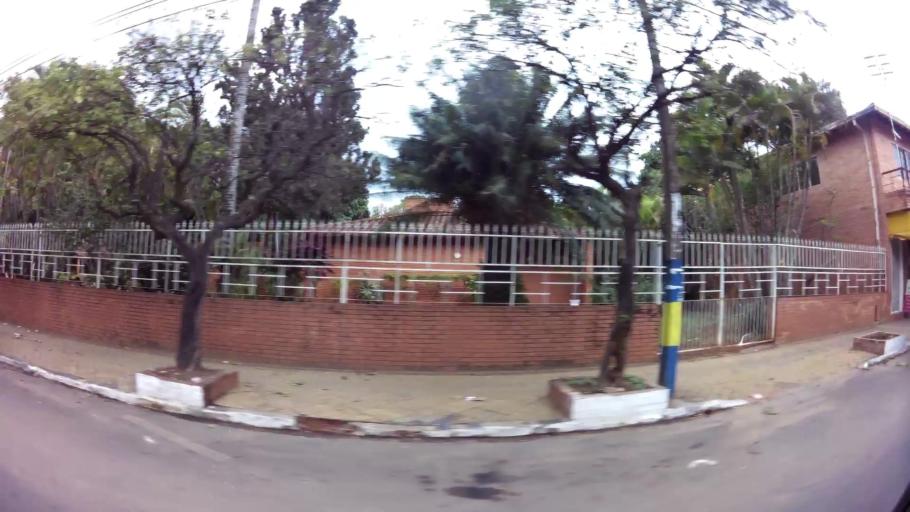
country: PY
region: Central
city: San Lorenzo
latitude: -25.2708
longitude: -57.4934
